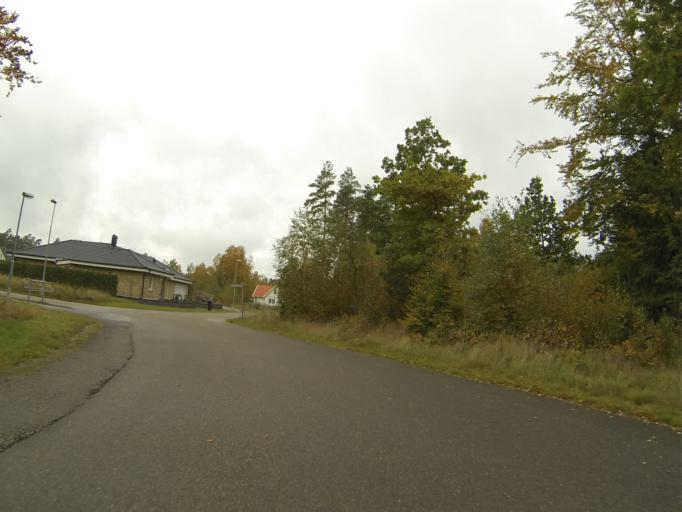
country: SE
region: Skane
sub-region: Sjobo Kommun
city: Sjoebo
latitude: 55.6377
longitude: 13.6725
